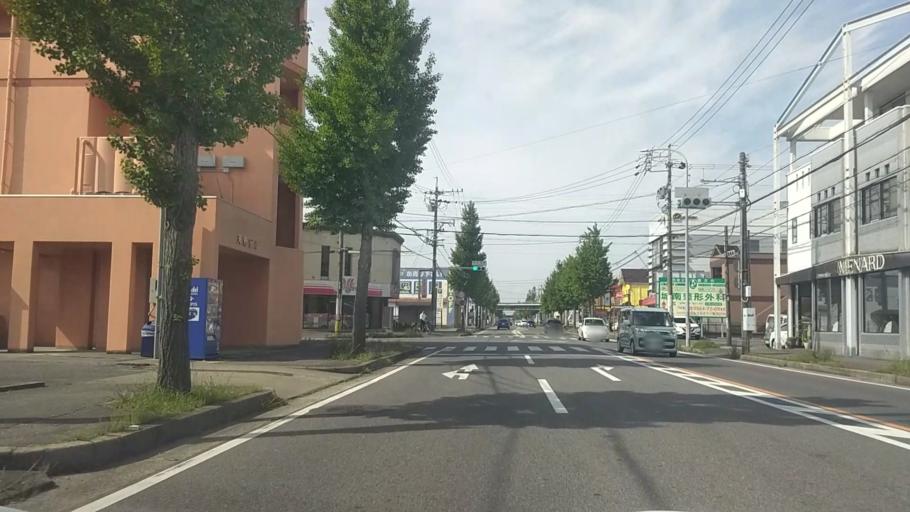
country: JP
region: Aichi
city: Okazaki
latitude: 34.9436
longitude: 137.1533
